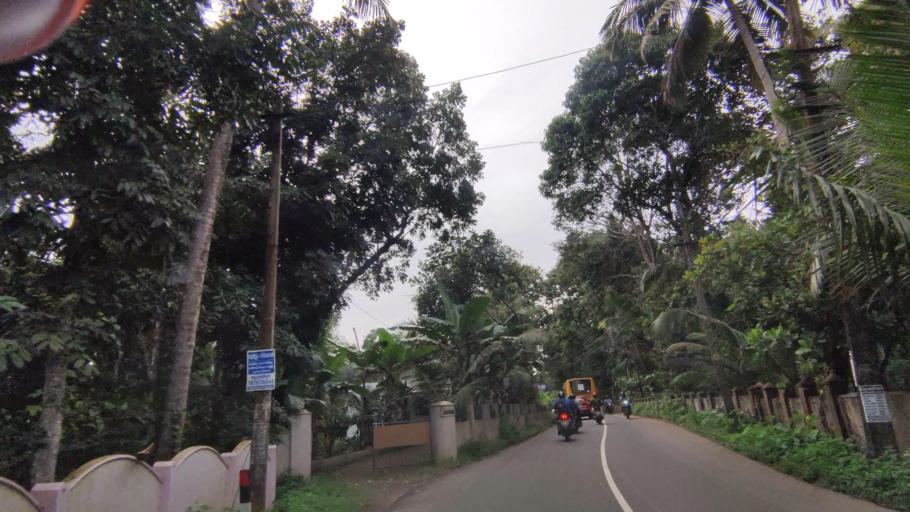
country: IN
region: Kerala
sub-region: Kottayam
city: Kottayam
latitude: 9.6879
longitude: 76.5021
